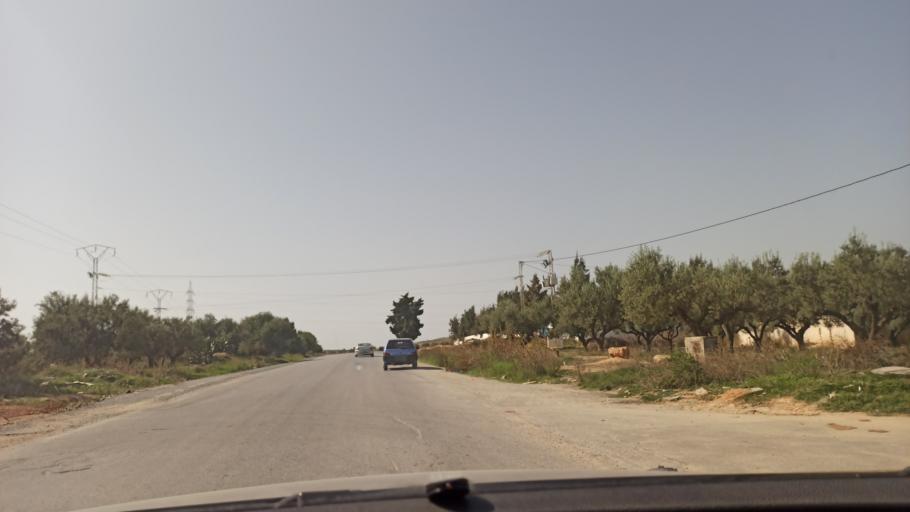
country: TN
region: Manouba
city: Manouba
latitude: 36.7495
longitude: 10.0990
